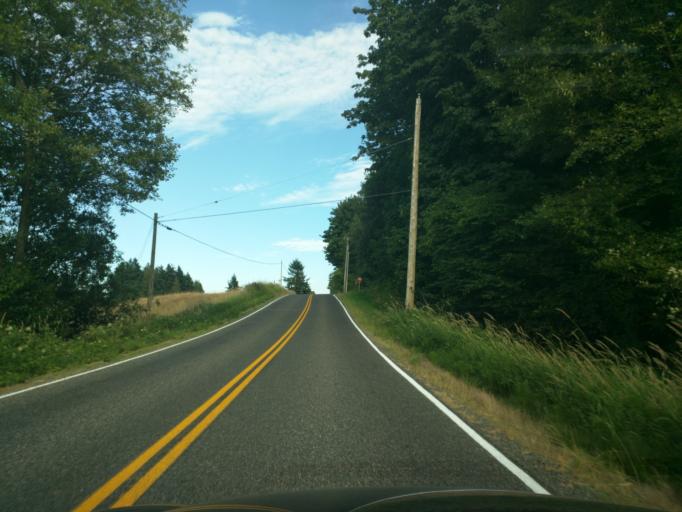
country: CA
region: British Columbia
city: Aldergrove
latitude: 48.9934
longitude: -122.5186
